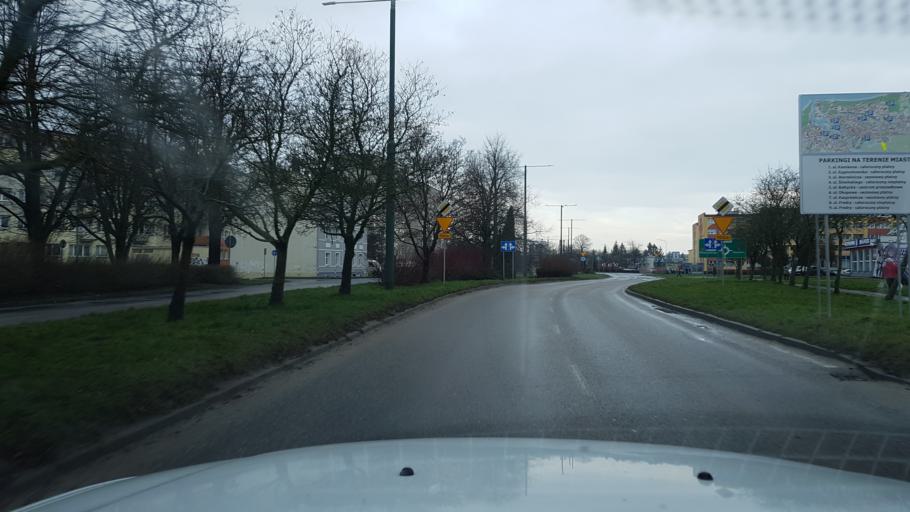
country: PL
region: West Pomeranian Voivodeship
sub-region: Powiat kolobrzeski
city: Kolobrzeg
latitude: 54.1745
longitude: 15.5884
